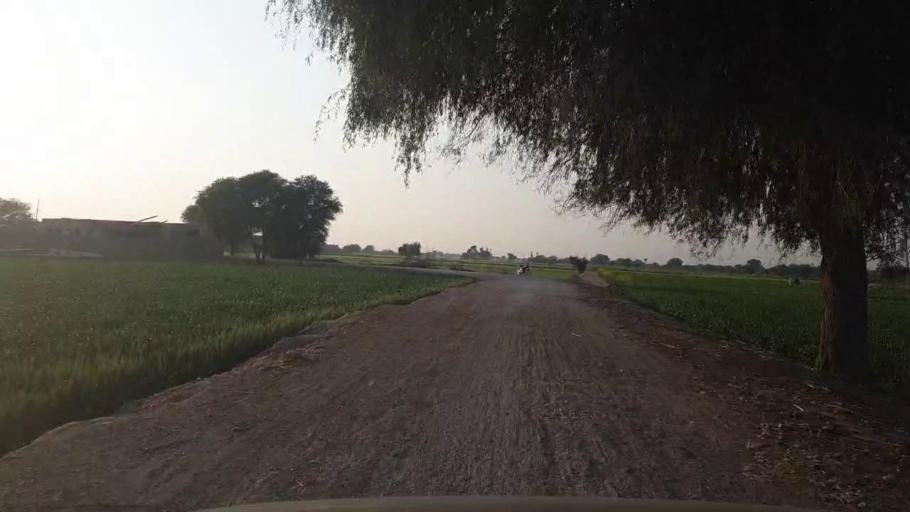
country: PK
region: Sindh
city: Hala
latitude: 25.8705
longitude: 68.4063
